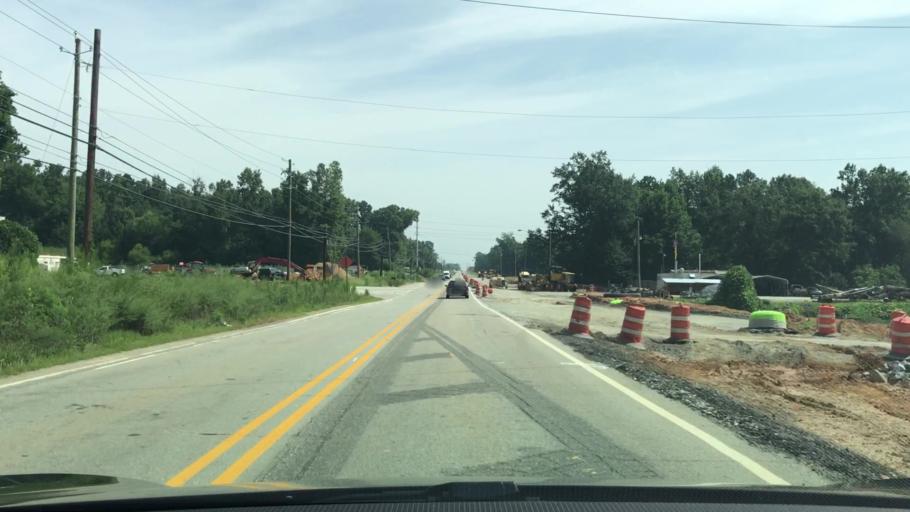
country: US
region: Georgia
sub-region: Gwinnett County
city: Buford
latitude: 34.1354
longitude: -83.9746
